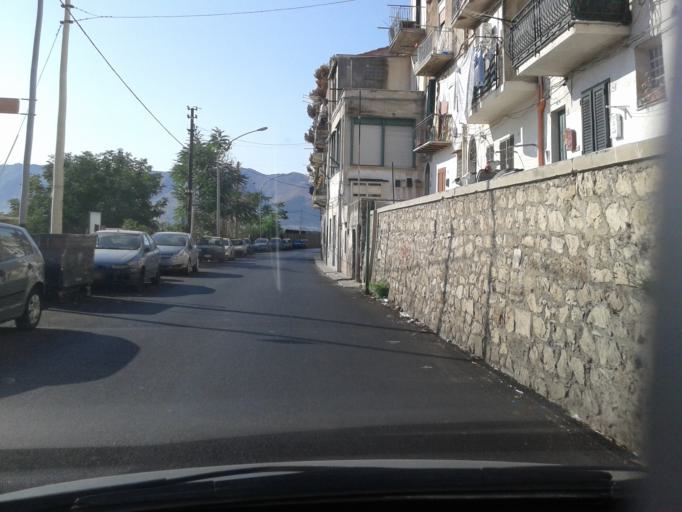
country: IT
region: Sicily
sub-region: Palermo
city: Monreale
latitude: 38.1071
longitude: 13.3095
